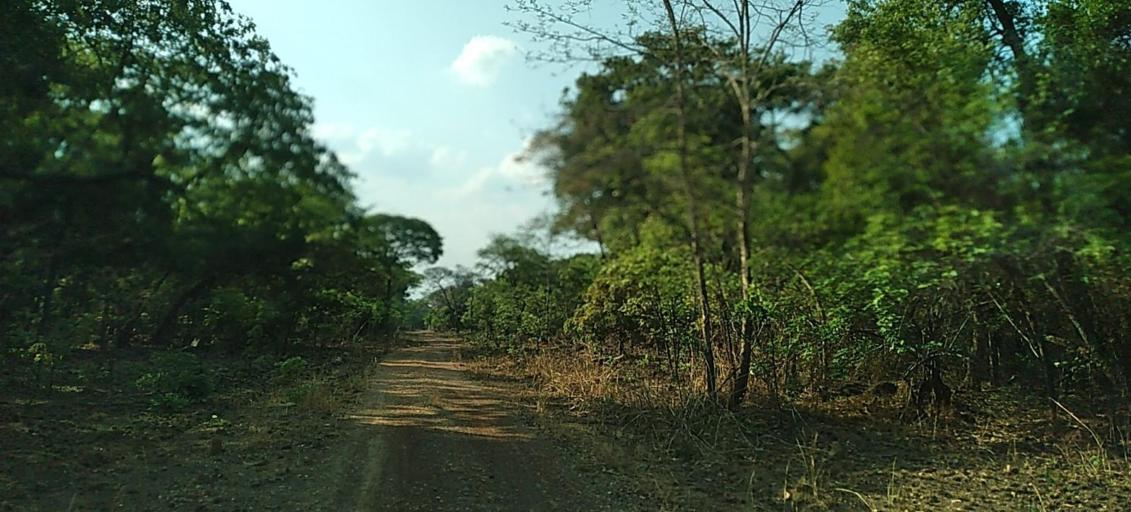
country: ZM
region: Copperbelt
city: Mpongwe
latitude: -13.3886
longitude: 28.0101
